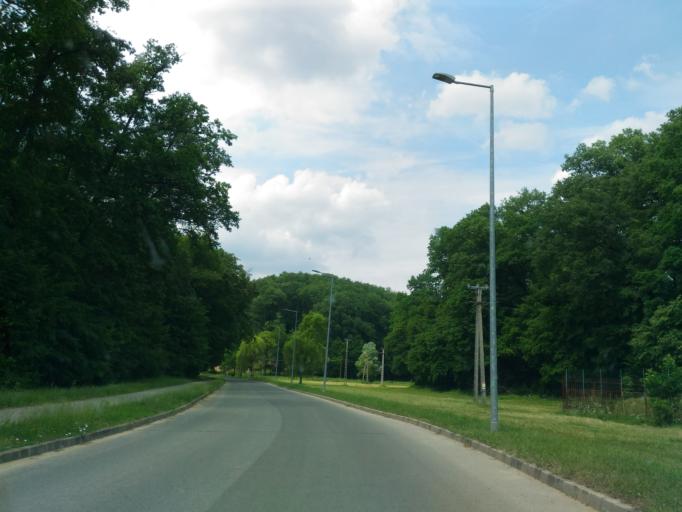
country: HU
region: Baranya
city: Komlo
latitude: 46.1788
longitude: 18.2203
